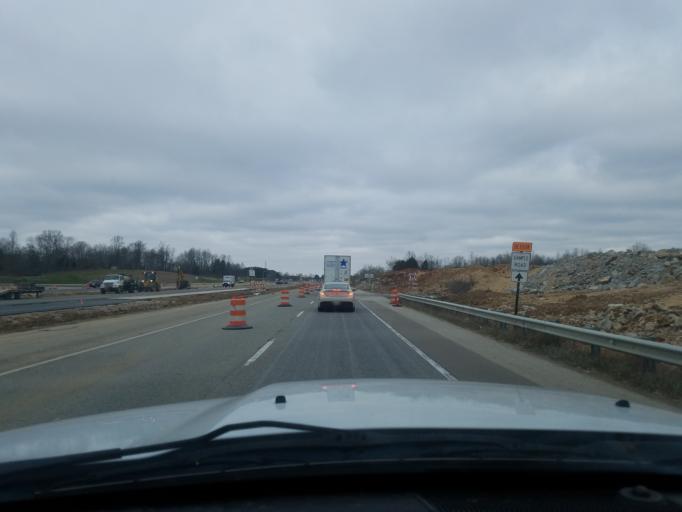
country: US
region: Indiana
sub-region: Monroe County
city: Bloomington
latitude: 39.2654
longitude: -86.5225
